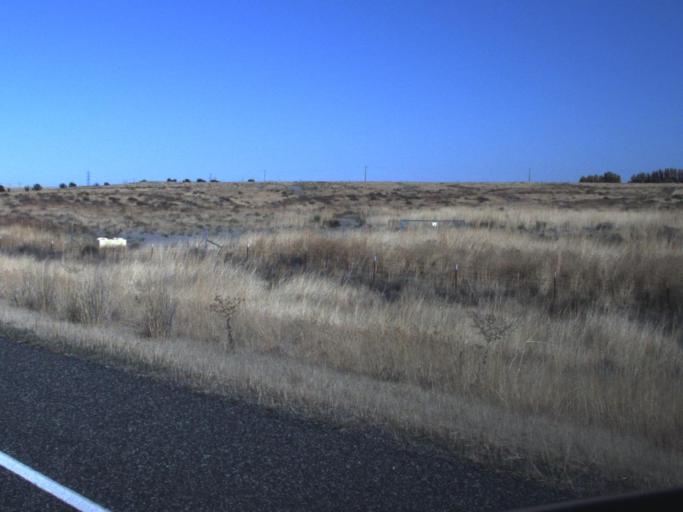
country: US
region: Washington
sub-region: Benton County
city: West Richland
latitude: 46.3447
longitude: -119.3521
